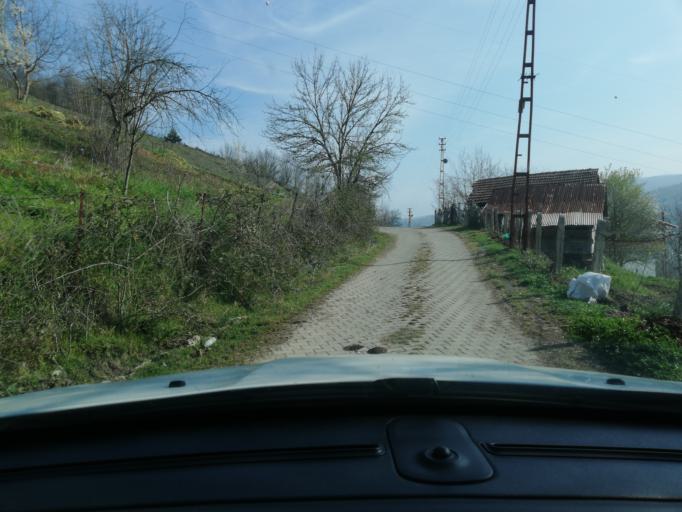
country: TR
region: Karabuk
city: Yenice
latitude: 41.2708
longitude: 32.3597
